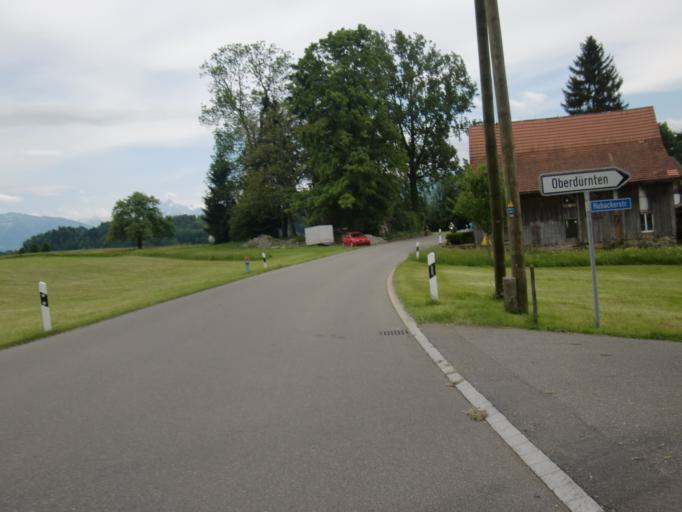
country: CH
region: Zurich
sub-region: Bezirk Hinwil
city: Rueti / Oberdorf
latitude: 47.2785
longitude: 8.8819
